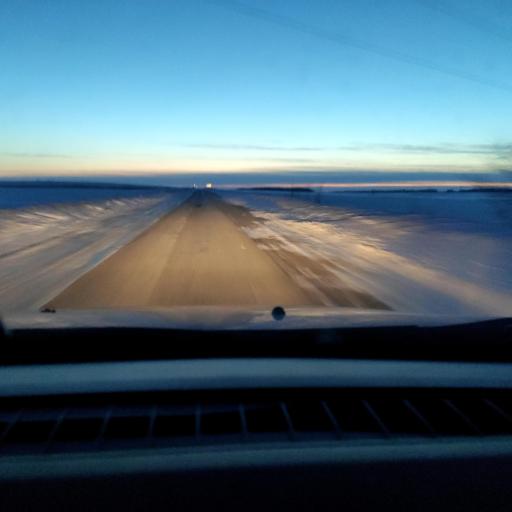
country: RU
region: Samara
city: Georgiyevka
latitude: 53.3083
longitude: 50.8210
